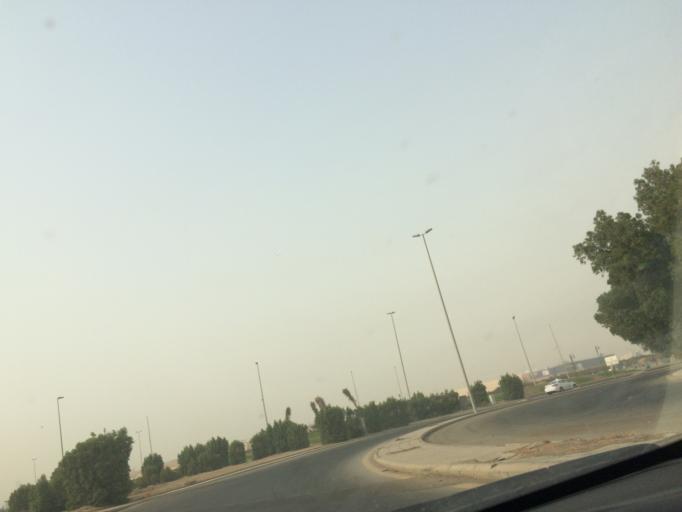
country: SA
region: Makkah
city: Jeddah
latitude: 21.4965
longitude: 39.2182
